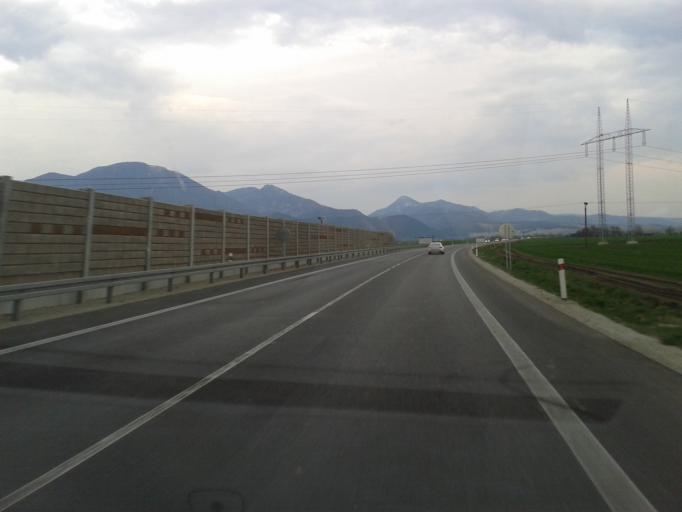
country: SK
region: Zilinsky
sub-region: Okres Martin
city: Martin
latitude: 48.9769
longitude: 18.9040
